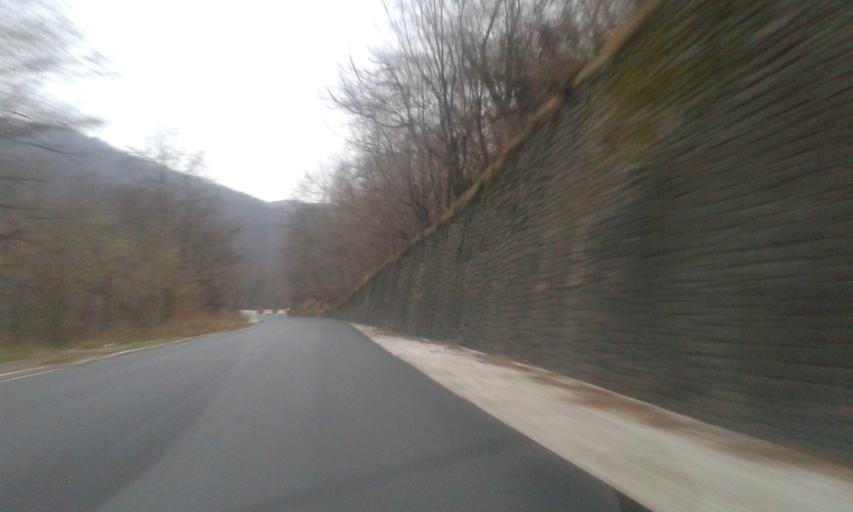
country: RO
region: Gorj
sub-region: Comuna Bumbesti-Jiu
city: Bumbesti-Jiu
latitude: 45.2704
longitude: 23.3850
